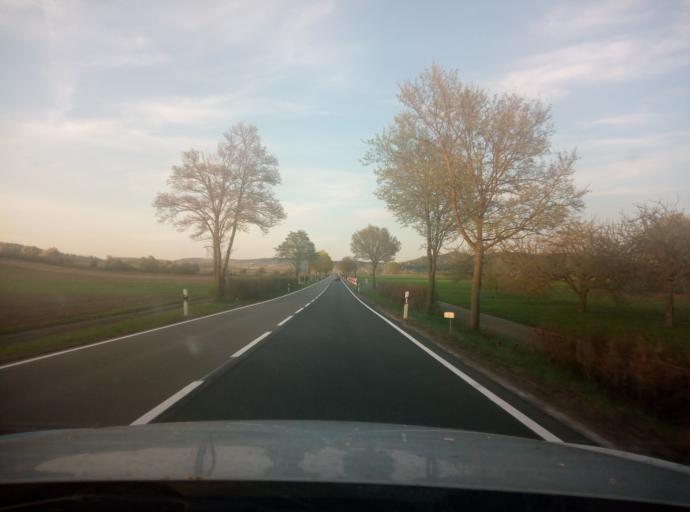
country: DE
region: Baden-Wuerttemberg
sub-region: Tuebingen Region
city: Rottenburg
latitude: 48.4887
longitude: 8.9513
